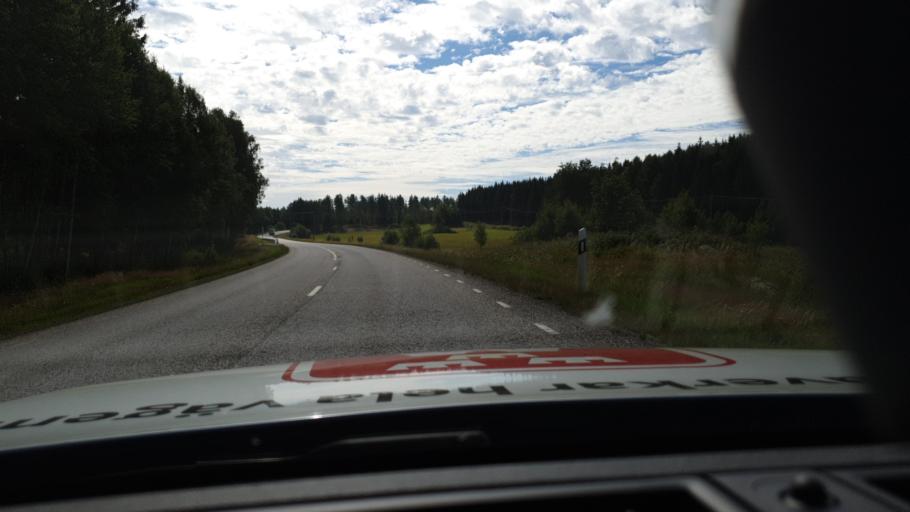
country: SE
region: Joenkoeping
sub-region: Vaggeryds Kommun
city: Vaggeryd
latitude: 57.5367
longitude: 14.2686
